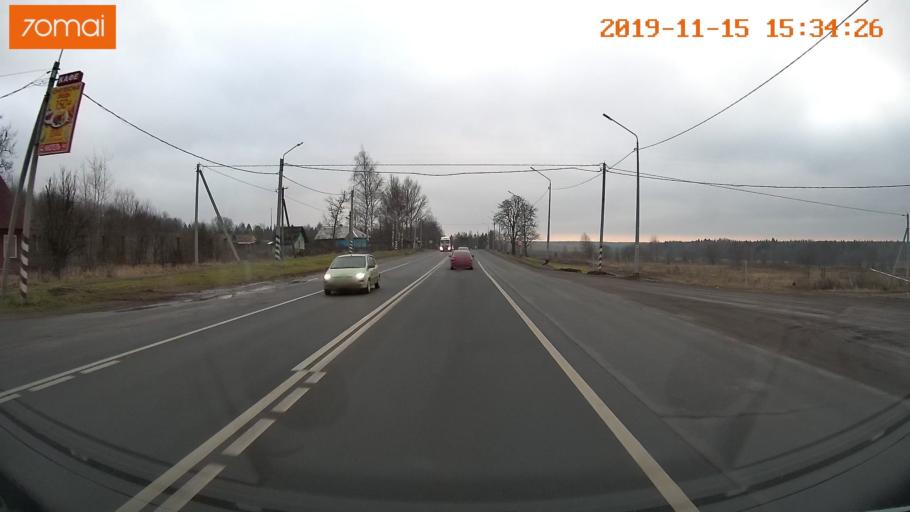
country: RU
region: Jaroslavl
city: Danilov
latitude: 58.0693
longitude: 40.0889
